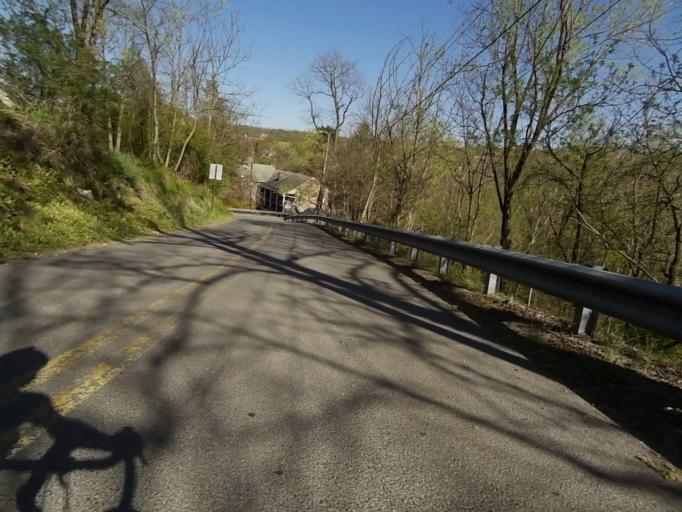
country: US
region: Pennsylvania
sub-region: Centre County
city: Bellefonte
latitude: 40.9072
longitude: -77.7876
